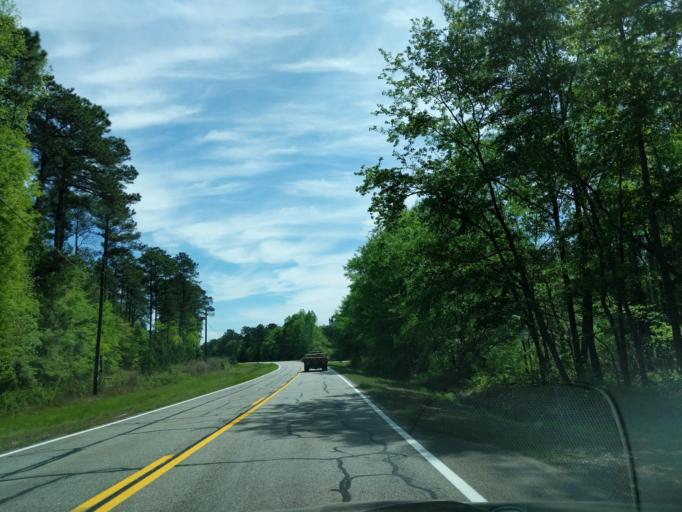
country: US
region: Georgia
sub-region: Columbia County
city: Appling
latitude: 33.6103
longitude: -82.3463
